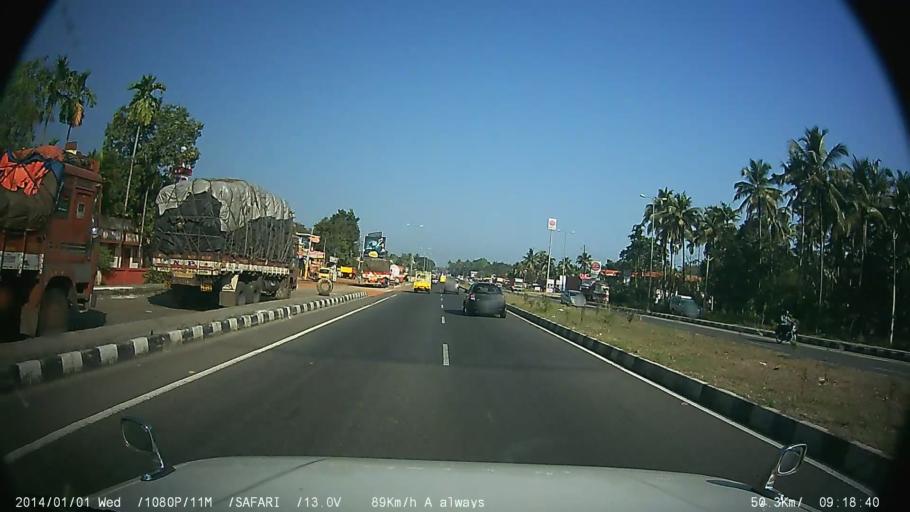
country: IN
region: Kerala
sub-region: Ernakulam
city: Angamali
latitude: 10.2483
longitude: 76.3693
